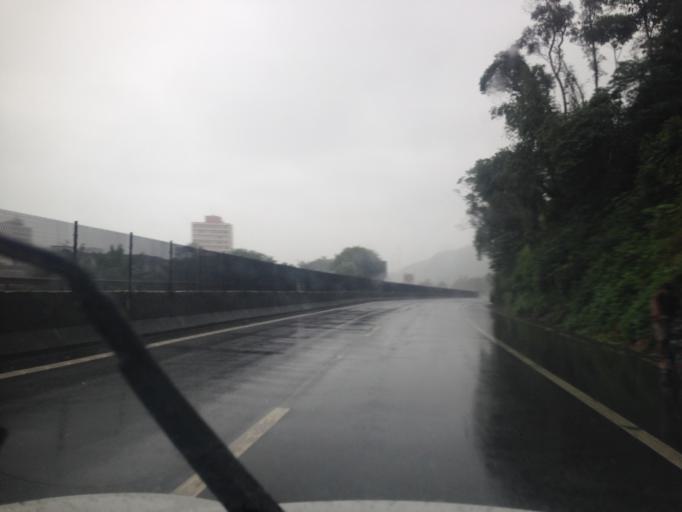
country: BR
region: Sao Paulo
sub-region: Mongagua
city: Mongagua
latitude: -24.0909
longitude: -46.6172
